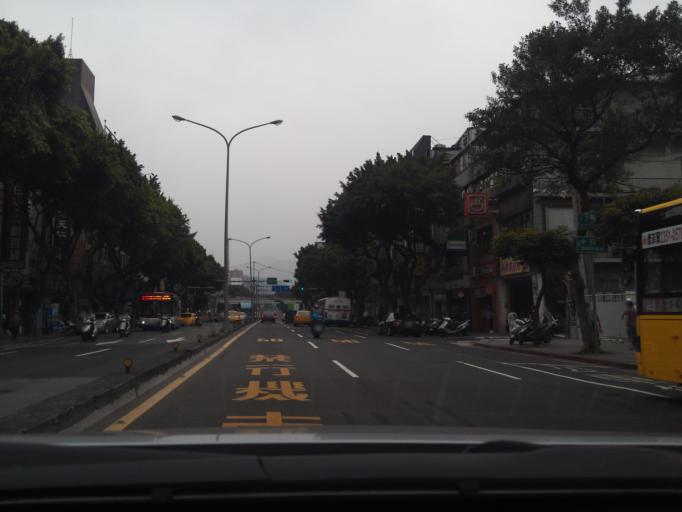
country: TW
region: Taipei
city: Taipei
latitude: 25.0946
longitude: 121.5226
